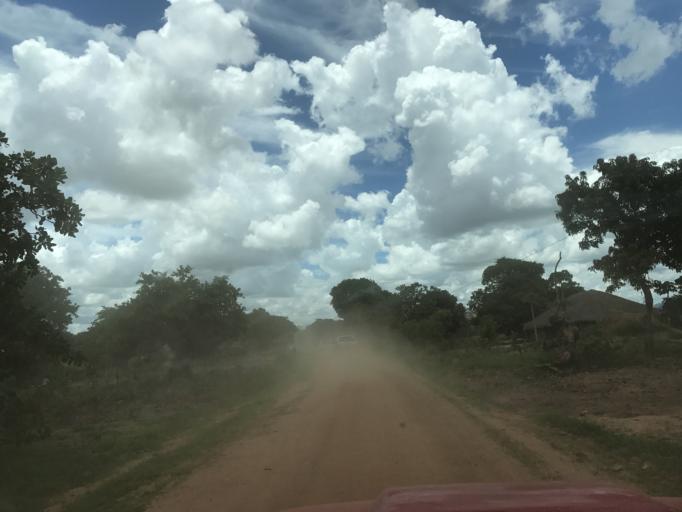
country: MZ
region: Nampula
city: Nacala
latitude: -13.9727
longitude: 40.1697
